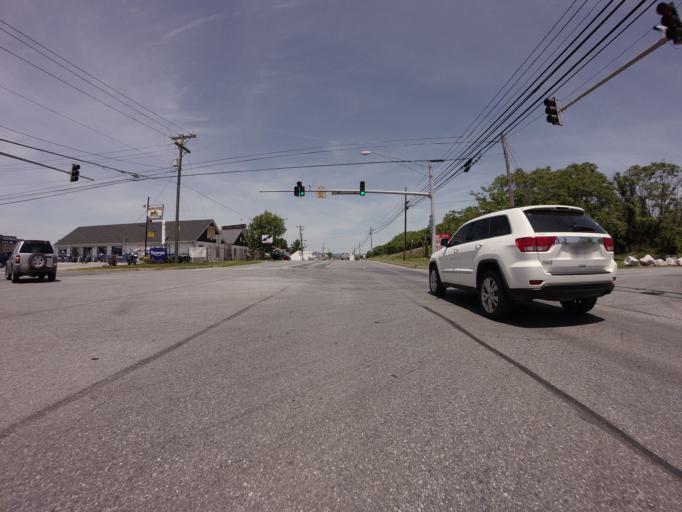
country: US
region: Maryland
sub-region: Frederick County
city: Frederick
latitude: 39.3912
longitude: -77.4052
